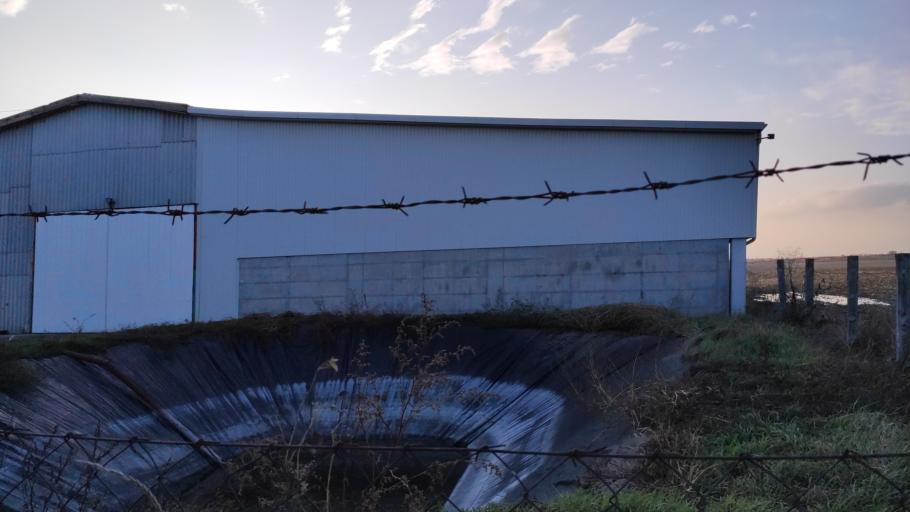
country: HU
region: Bekes
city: Mezobereny
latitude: 46.7666
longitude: 21.0445
